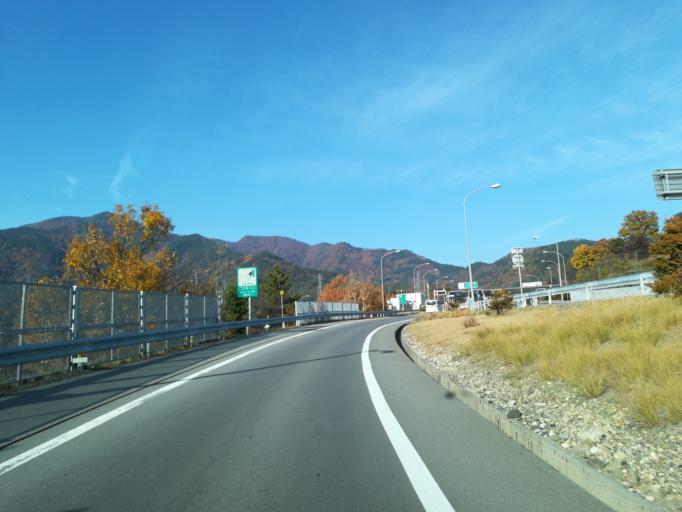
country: JP
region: Nagano
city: Ueda
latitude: 36.4090
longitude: 138.2803
